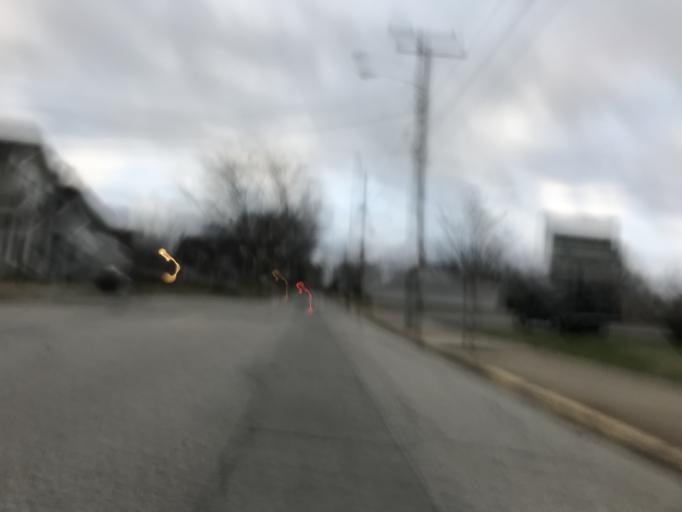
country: US
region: Kentucky
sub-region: Jefferson County
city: Louisville
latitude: 38.2362
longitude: -85.7451
